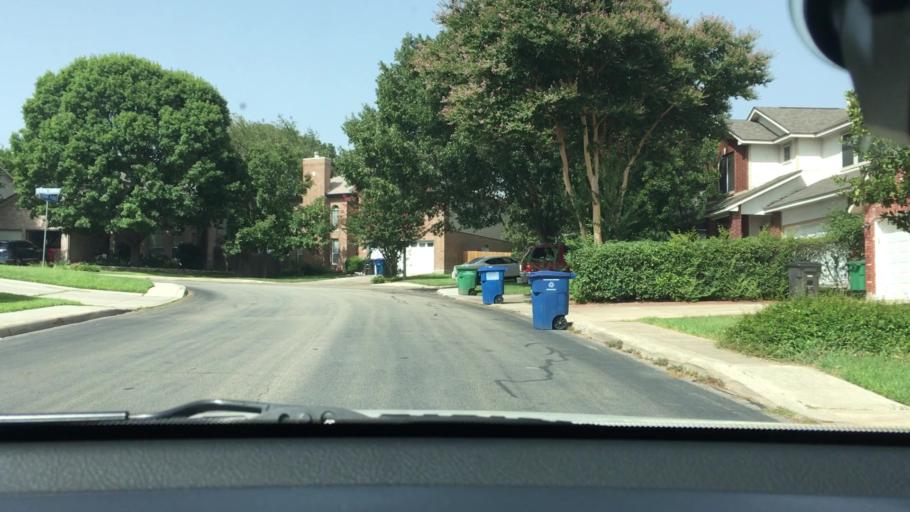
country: US
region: Texas
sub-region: Bexar County
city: Live Oak
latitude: 29.5814
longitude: -98.3828
